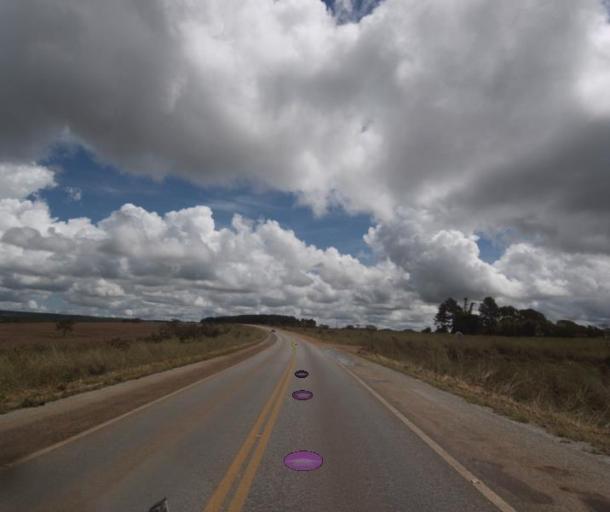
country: BR
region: Goias
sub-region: Pirenopolis
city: Pirenopolis
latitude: -15.7485
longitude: -48.6653
